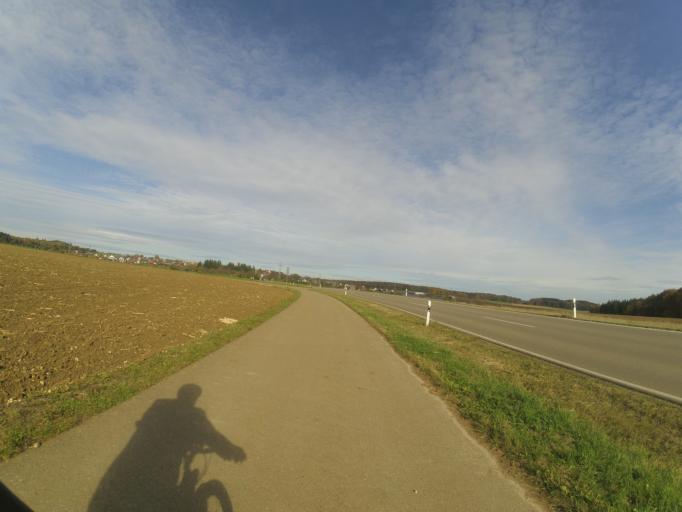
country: DE
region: Baden-Wuerttemberg
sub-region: Tuebingen Region
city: Lonsee
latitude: 48.5883
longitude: 9.9204
